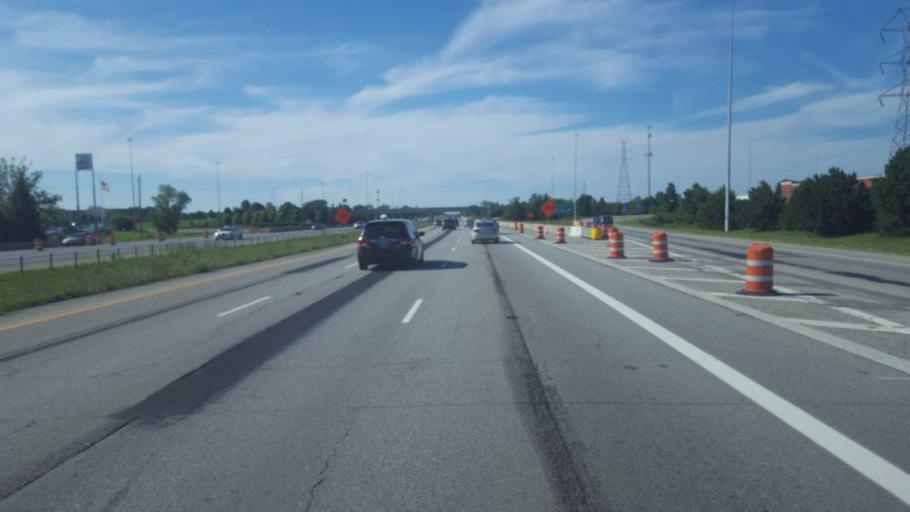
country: US
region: Ohio
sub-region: Franklin County
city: Hilliard
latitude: 40.0300
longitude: -83.1228
